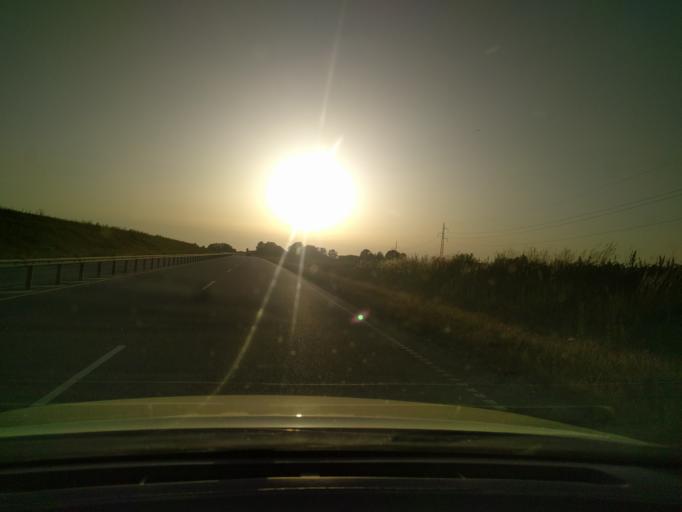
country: DK
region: Zealand
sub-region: Naestved Kommune
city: Fensmark
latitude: 55.2594
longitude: 11.7990
